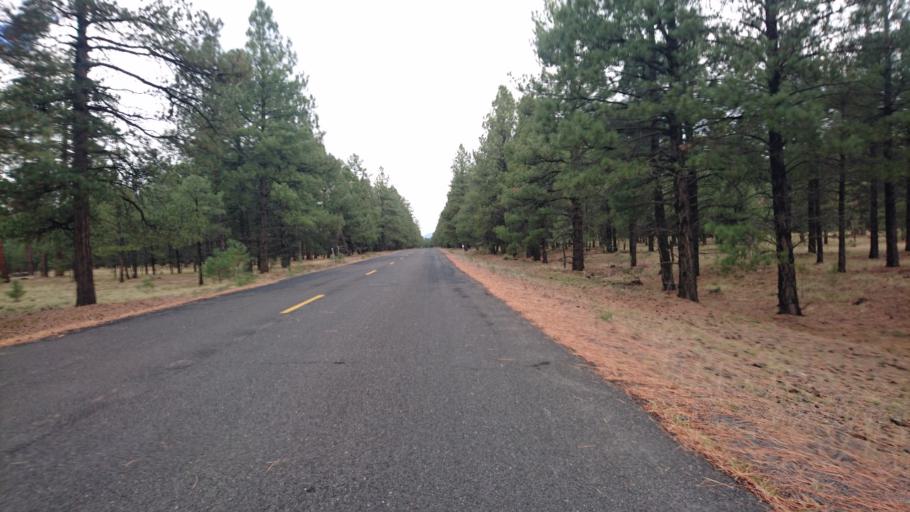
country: US
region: Arizona
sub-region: Coconino County
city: Parks
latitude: 35.2580
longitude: -111.8676
